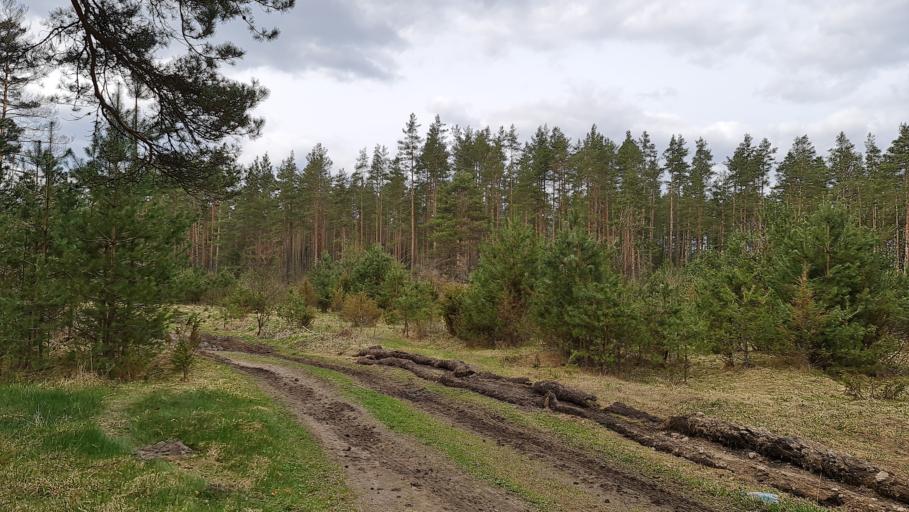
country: BY
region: Vitebsk
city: Byahoml'
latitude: 54.7396
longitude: 28.0321
